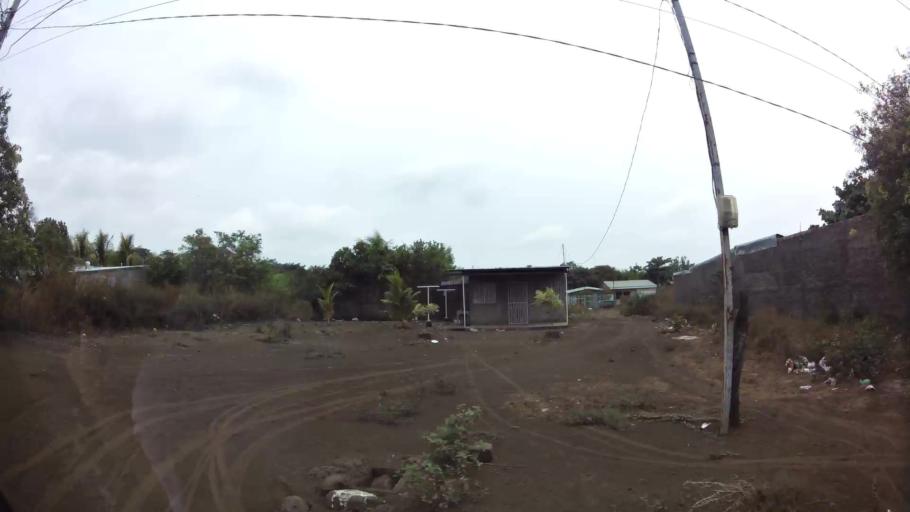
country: NI
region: Chinandega
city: Chinandega
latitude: 12.6240
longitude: -87.1123
